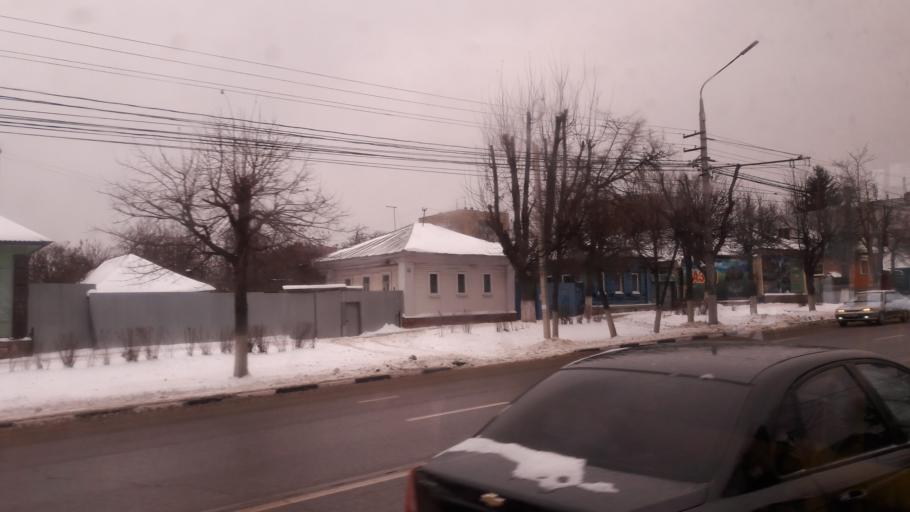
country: RU
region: Tula
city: Tula
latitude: 54.2239
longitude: 37.6278
